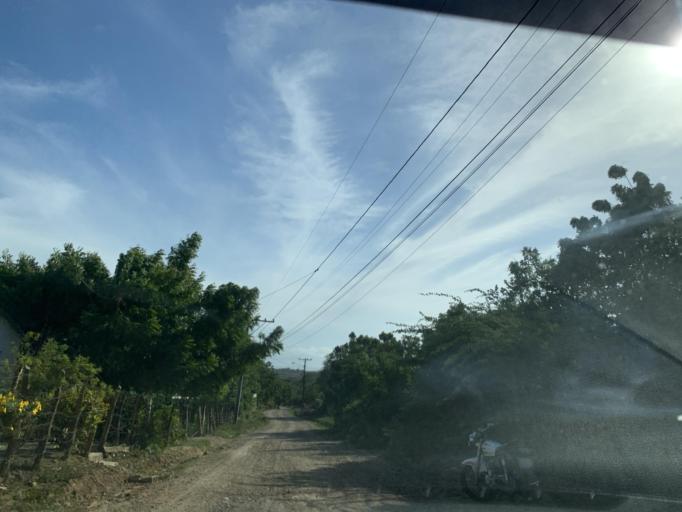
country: DO
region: Puerto Plata
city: Luperon
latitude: 19.8839
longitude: -70.9218
